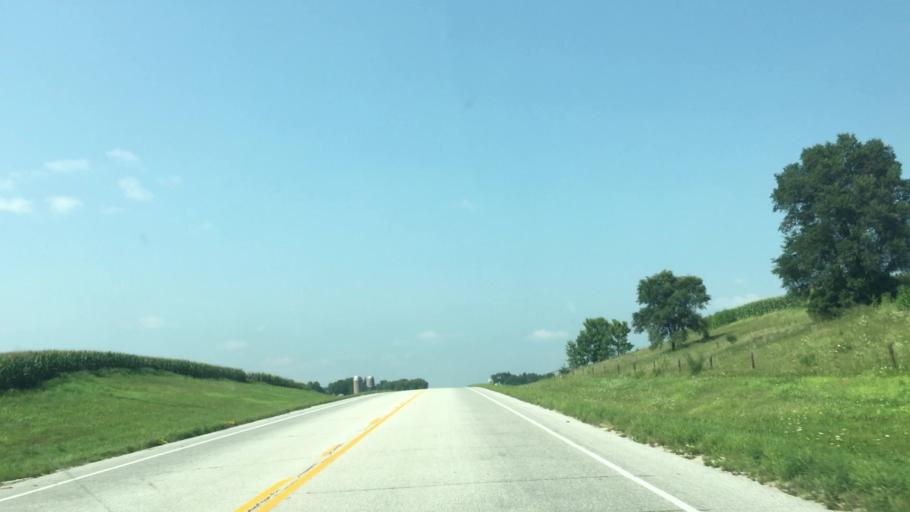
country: US
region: Minnesota
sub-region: Fillmore County
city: Harmony
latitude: 43.6078
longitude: -91.9297
